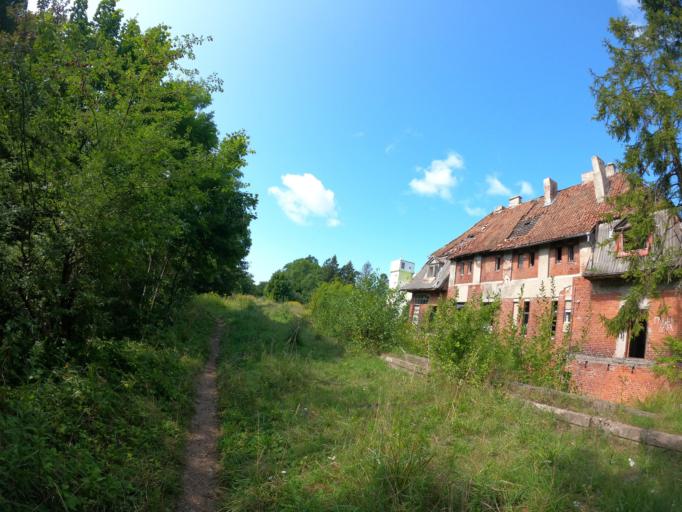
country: RU
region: Kaliningrad
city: Otradnoye
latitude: 54.9375
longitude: 20.1133
